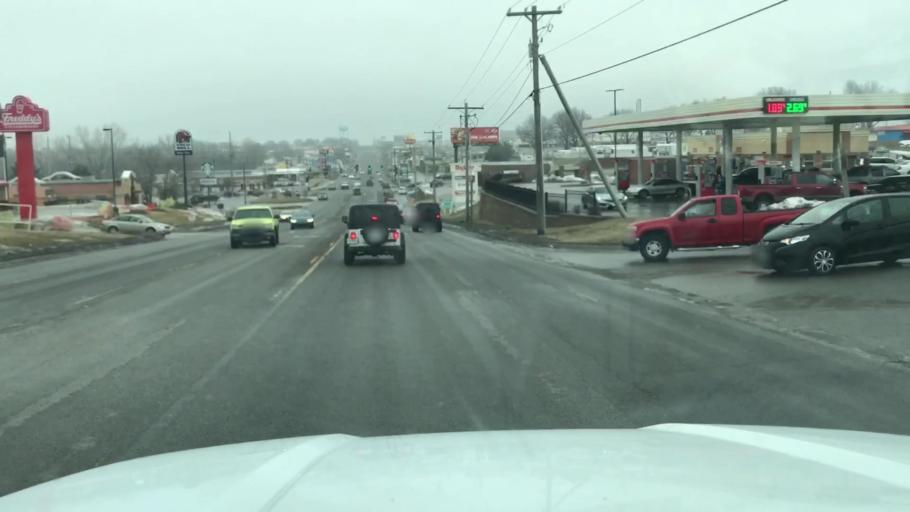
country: US
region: Missouri
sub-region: Buchanan County
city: Saint Joseph
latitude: 39.7675
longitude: -94.8036
